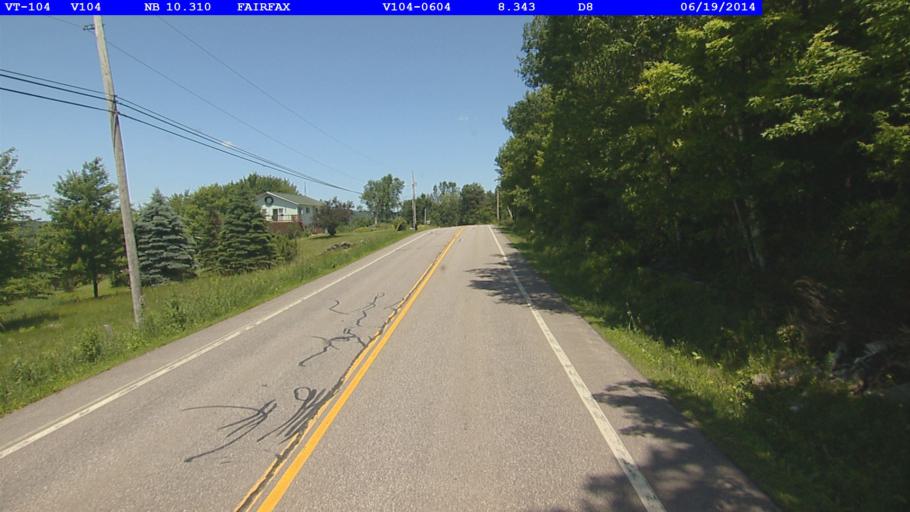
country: US
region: Vermont
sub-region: Chittenden County
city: Milton
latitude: 44.7048
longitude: -73.0365
